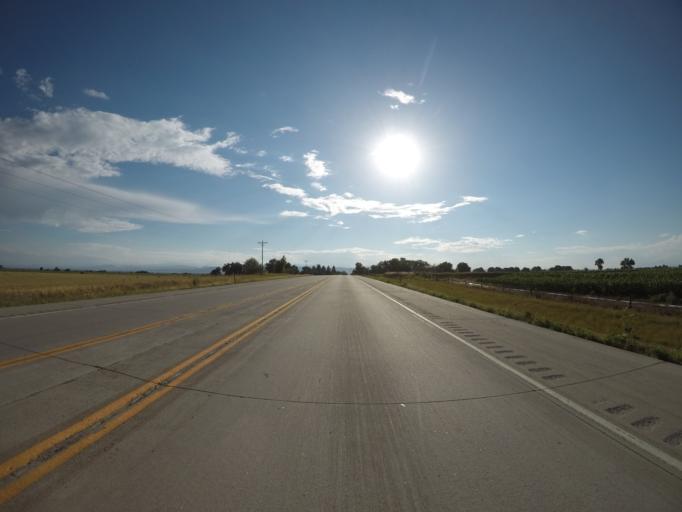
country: US
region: Colorado
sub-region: Weld County
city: Severance
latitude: 40.5810
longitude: -104.9474
